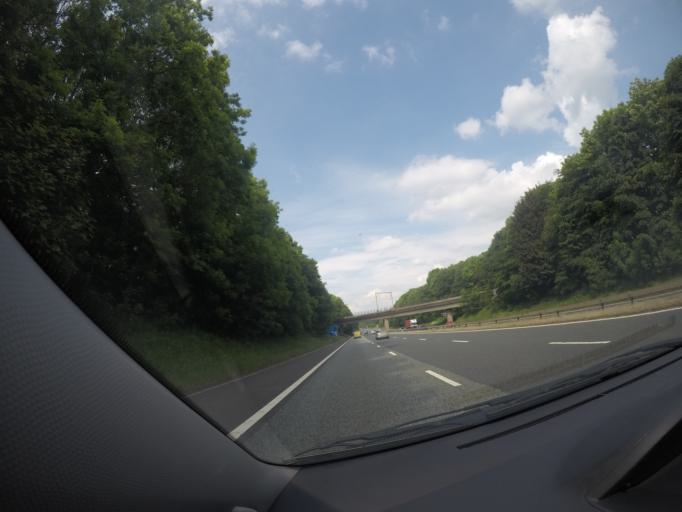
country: GB
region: England
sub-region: Cumbria
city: Scotby
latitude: 54.8439
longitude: -2.8854
